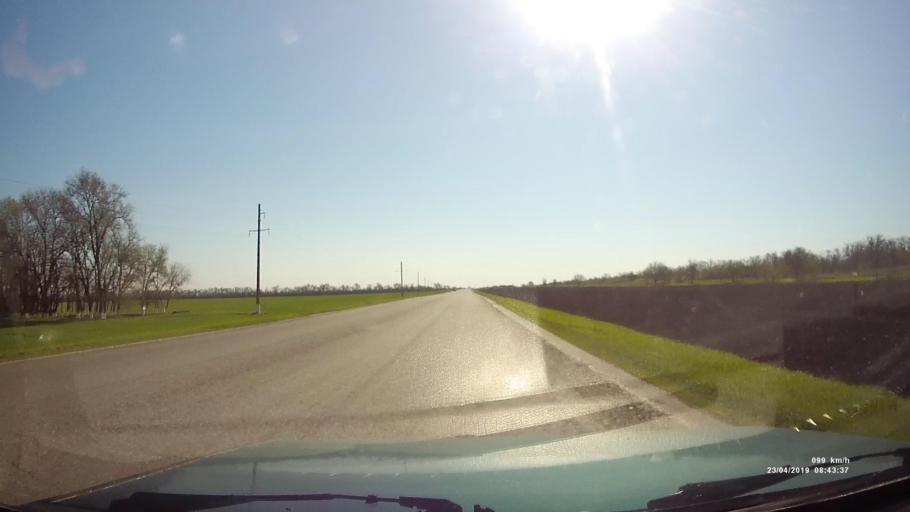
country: RU
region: Rostov
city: Gigant
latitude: 46.5221
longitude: 41.2949
